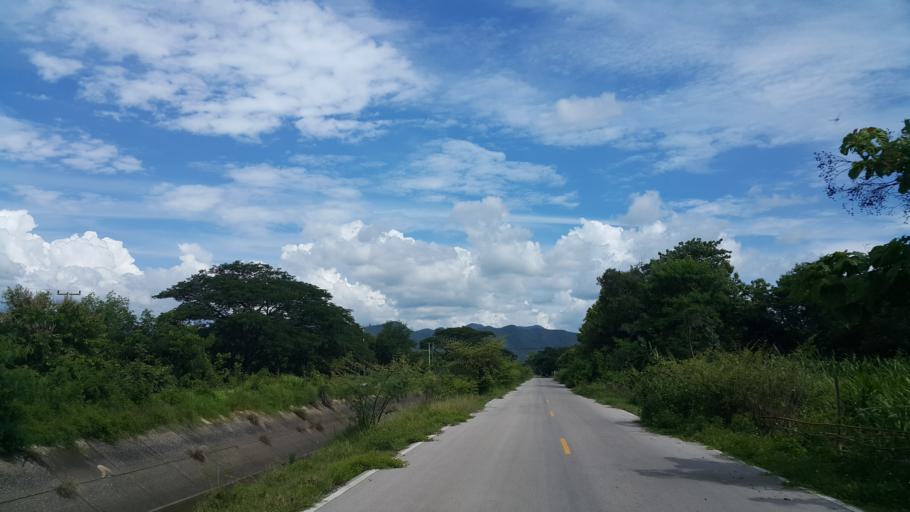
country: TH
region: Chiang Mai
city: Mae On
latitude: 18.7451
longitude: 99.2002
